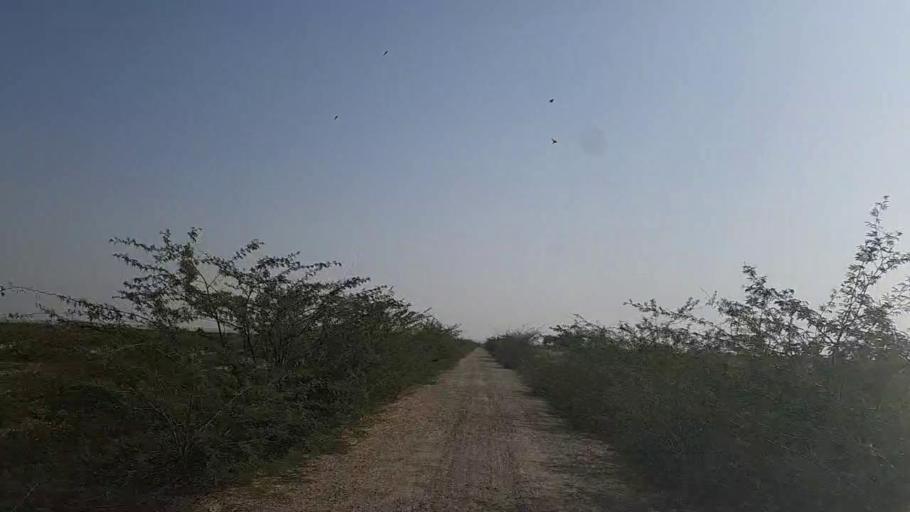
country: PK
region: Sindh
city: Kadhan
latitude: 24.5900
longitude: 69.2627
